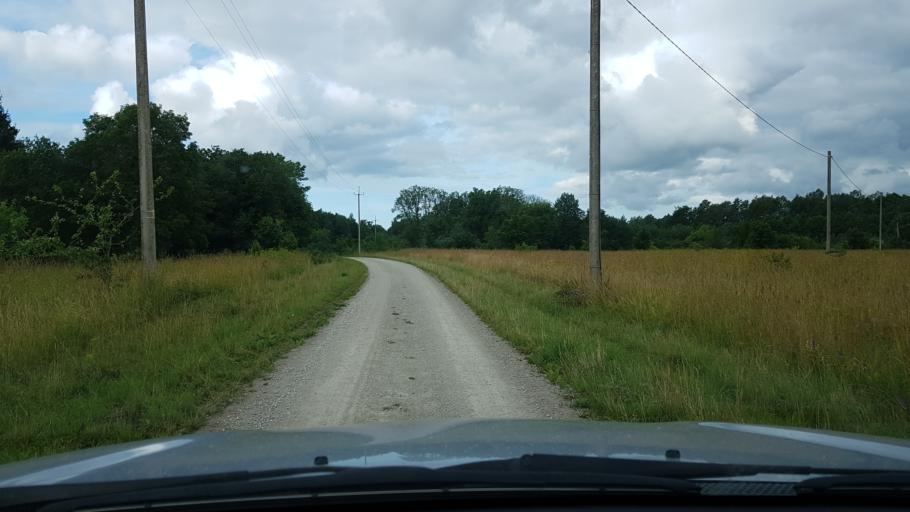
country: EE
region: Ida-Virumaa
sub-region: Narva-Joesuu linn
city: Narva-Joesuu
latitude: 59.4091
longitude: 27.9830
